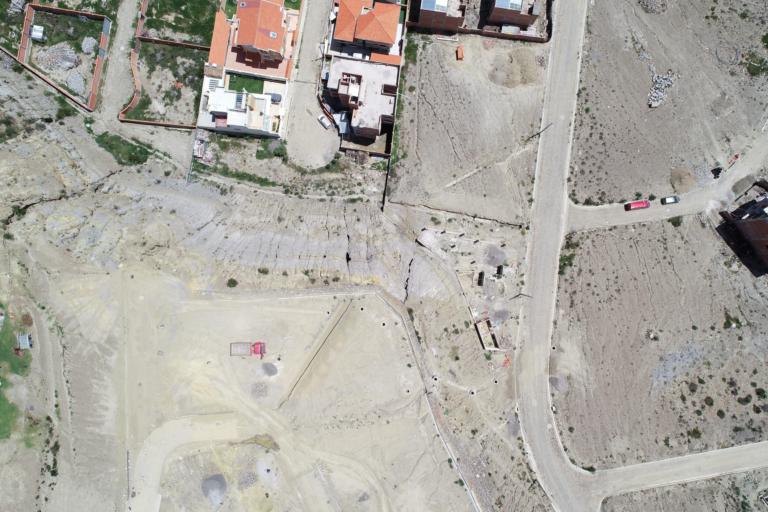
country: BO
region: La Paz
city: La Paz
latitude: -16.5235
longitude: -68.0501
